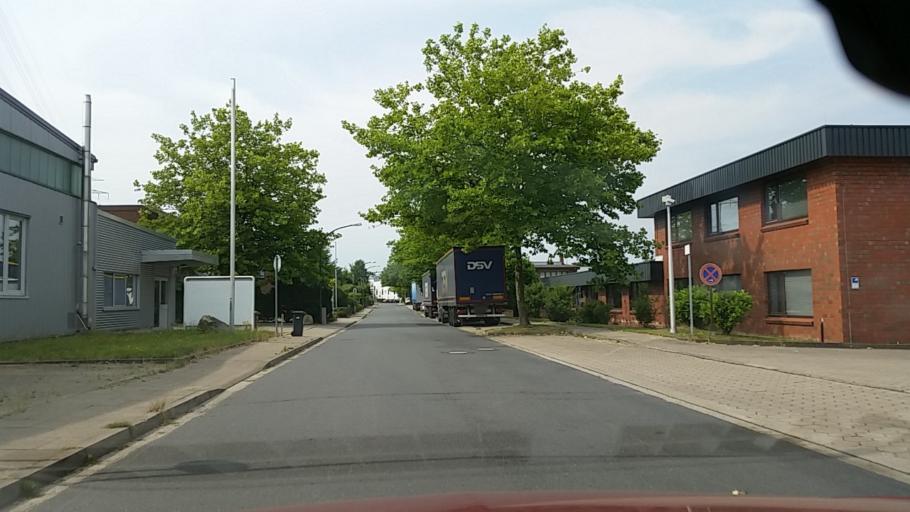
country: DE
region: Schleswig-Holstein
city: Oststeinbek
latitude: 53.5511
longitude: 10.1564
